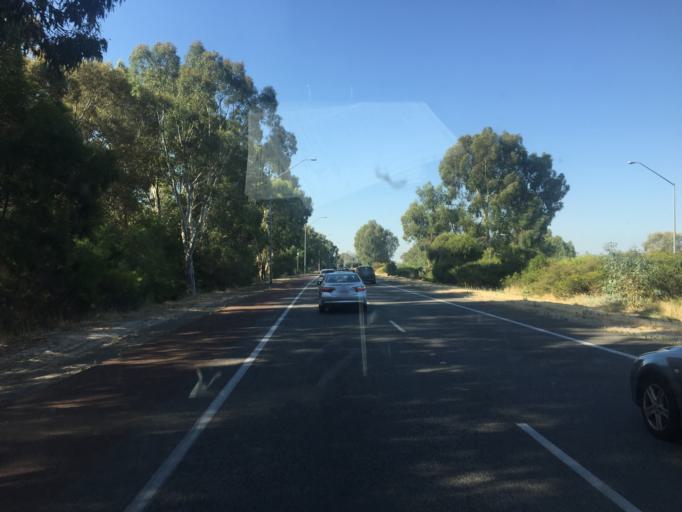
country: AU
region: Western Australia
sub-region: Gosnells
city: Kenwick
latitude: -32.0165
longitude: 115.9717
